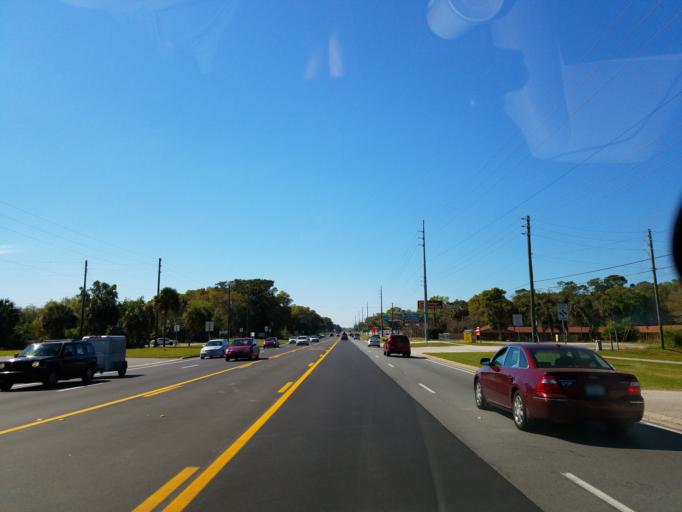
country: US
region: Florida
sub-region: Marion County
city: Ocala
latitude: 29.2078
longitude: -82.1875
